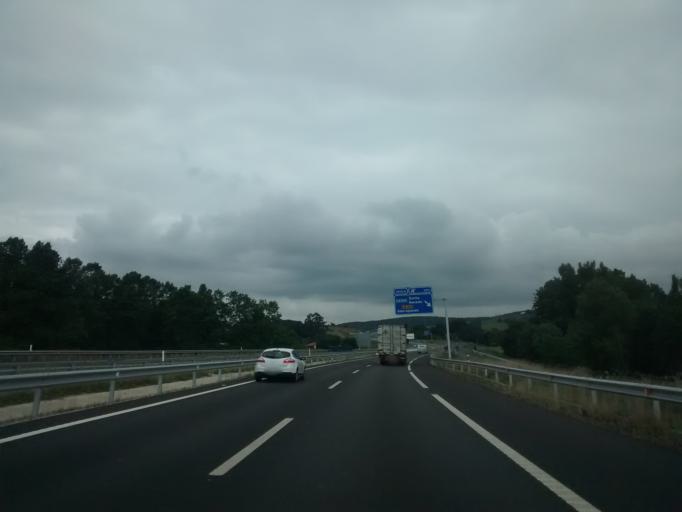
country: ES
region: Cantabria
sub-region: Provincia de Cantabria
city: Puente Viesgo
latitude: 43.3343
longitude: -3.9817
